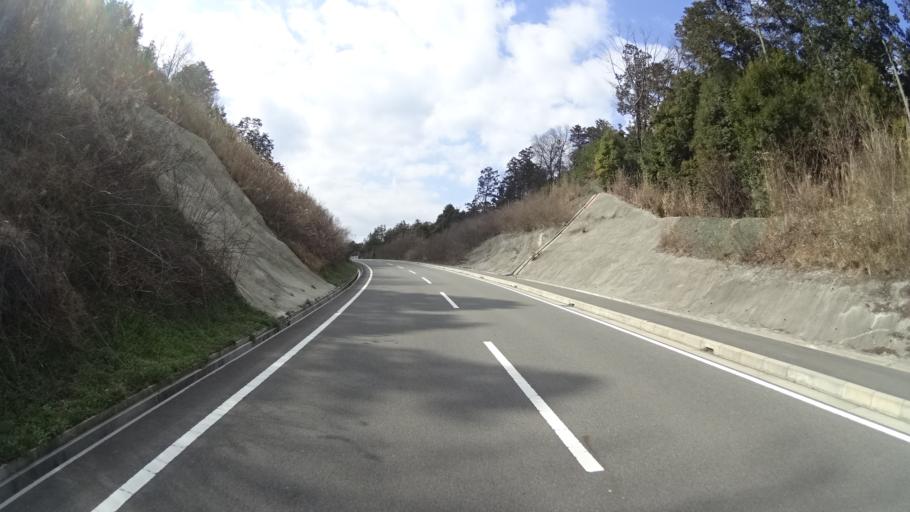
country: JP
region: Kyoto
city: Uji
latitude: 34.8410
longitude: 135.8490
